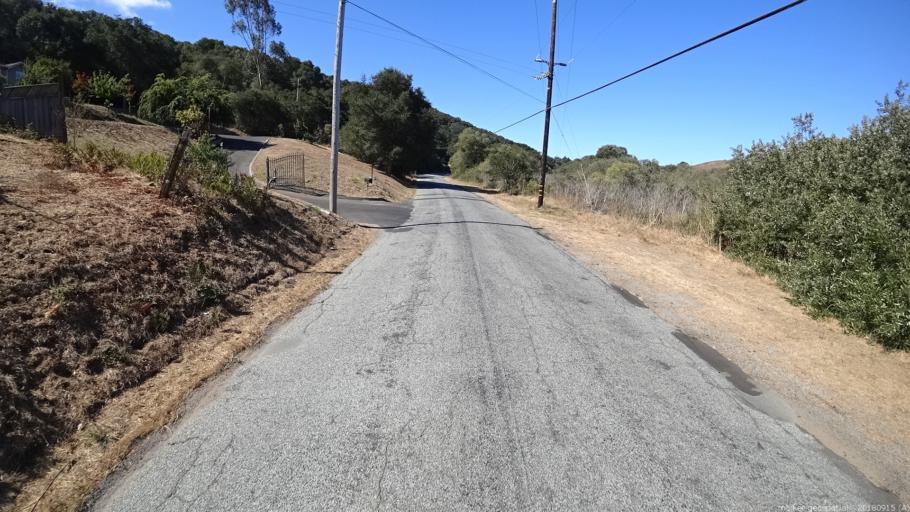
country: US
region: California
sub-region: Monterey County
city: Las Lomas
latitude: 36.8813
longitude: -121.7362
